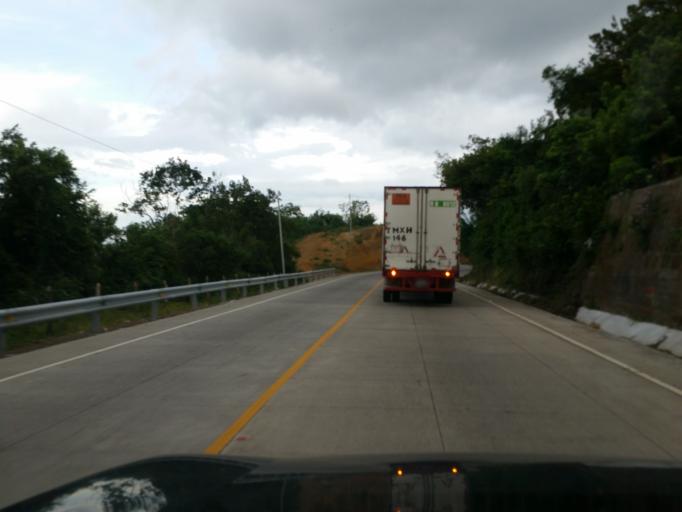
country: NI
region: Managua
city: Ciudad Sandino
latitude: 12.0831
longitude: -86.3797
